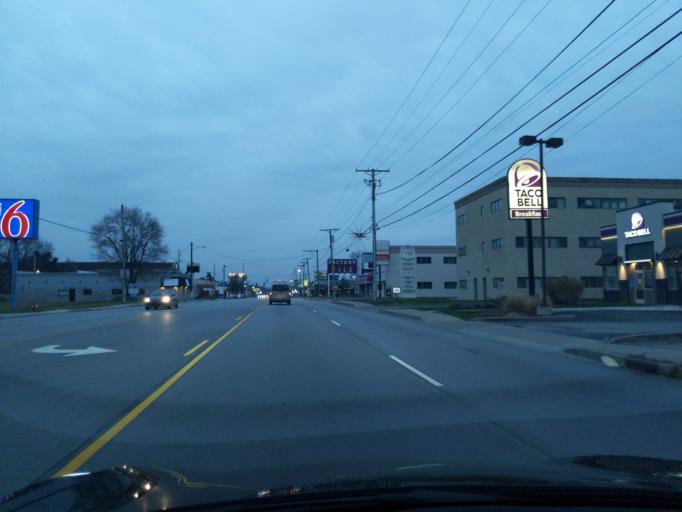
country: US
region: Indiana
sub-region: Saint Joseph County
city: Notre Dame
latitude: 41.7185
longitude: -86.2505
